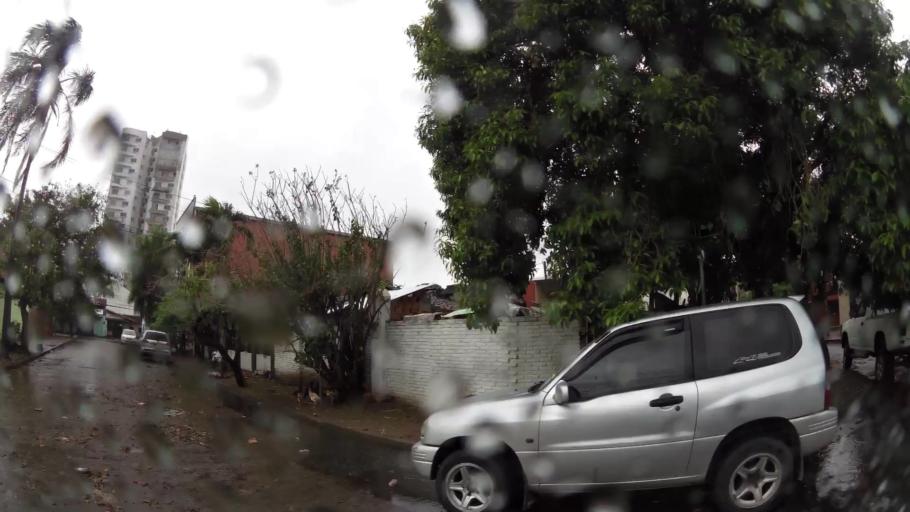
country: BO
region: Santa Cruz
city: Santa Cruz de la Sierra
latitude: -17.7806
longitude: -63.1959
